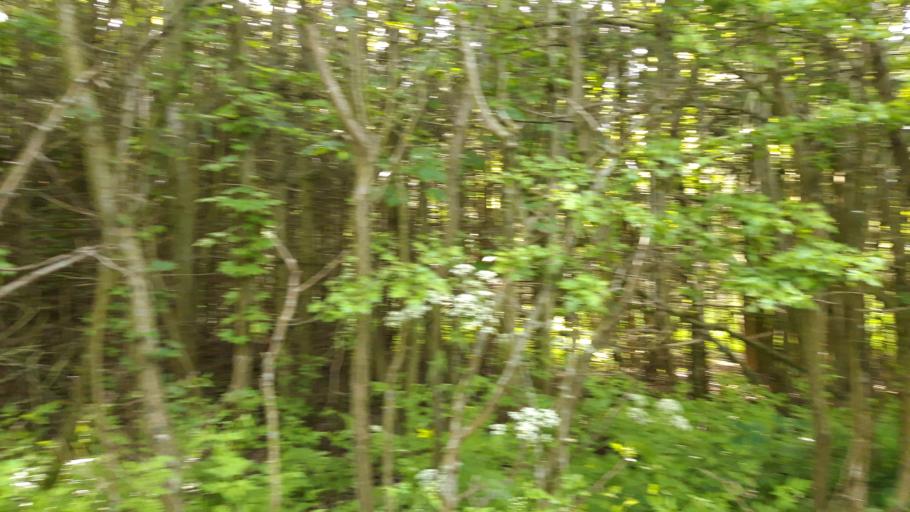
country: DK
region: Central Jutland
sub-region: Arhus Kommune
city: Lystrup
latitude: 56.2270
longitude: 10.1958
